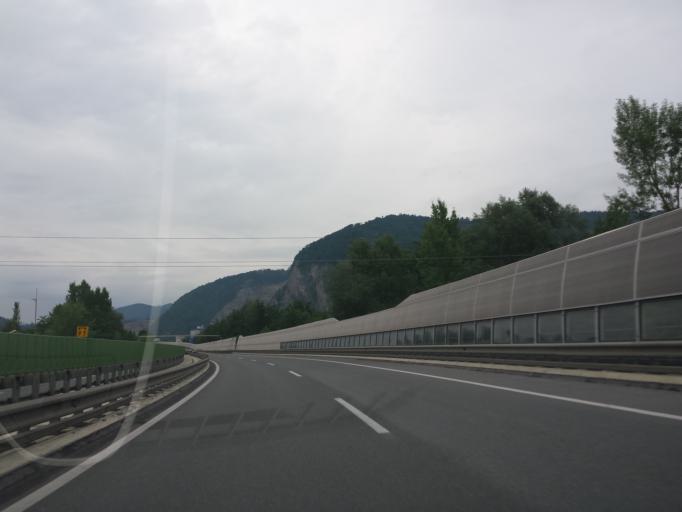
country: AT
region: Styria
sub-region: Politischer Bezirk Graz-Umgebung
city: Peggau
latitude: 47.1942
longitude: 15.3457
